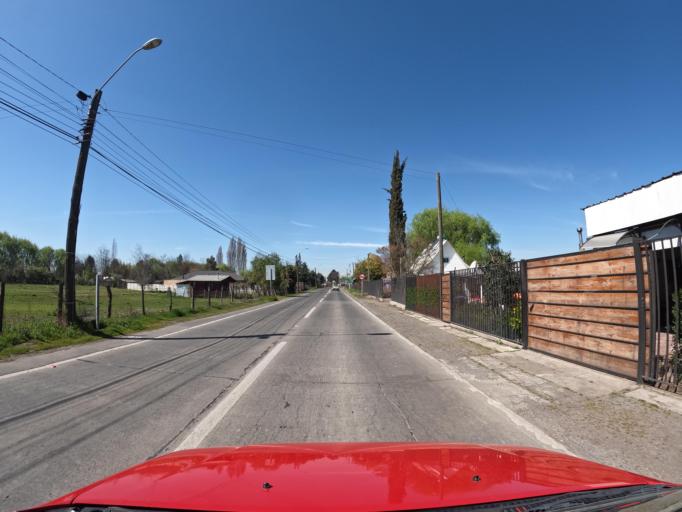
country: CL
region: Maule
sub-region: Provincia de Curico
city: Rauco
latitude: -35.0045
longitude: -71.3240
